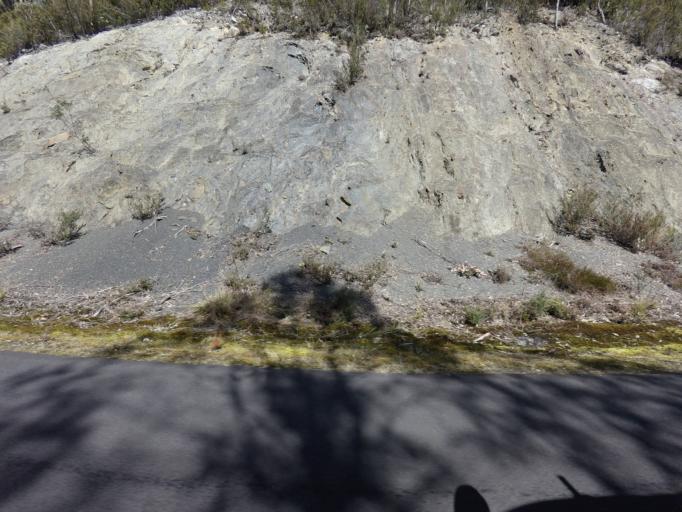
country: AU
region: Tasmania
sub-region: Derwent Valley
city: New Norfolk
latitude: -42.7288
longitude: 146.4666
